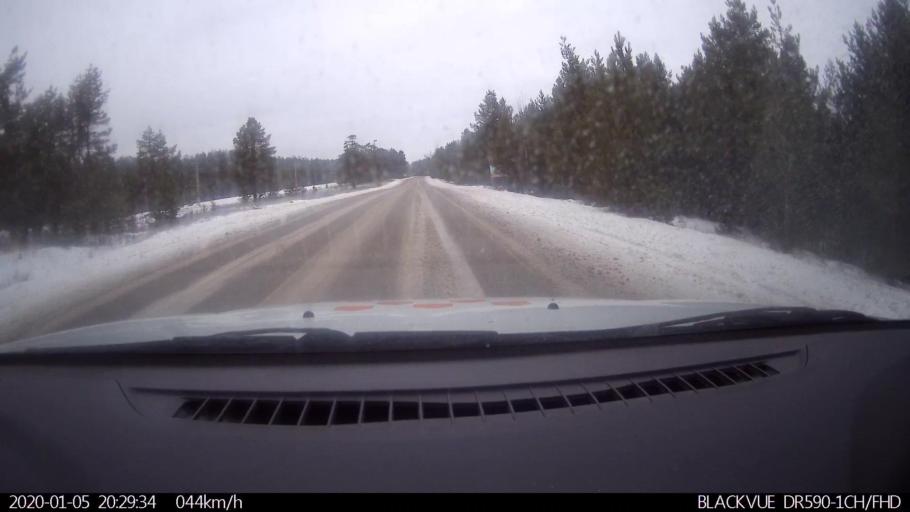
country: RU
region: Nizjnij Novgorod
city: Lukino
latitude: 56.3944
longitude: 43.7338
